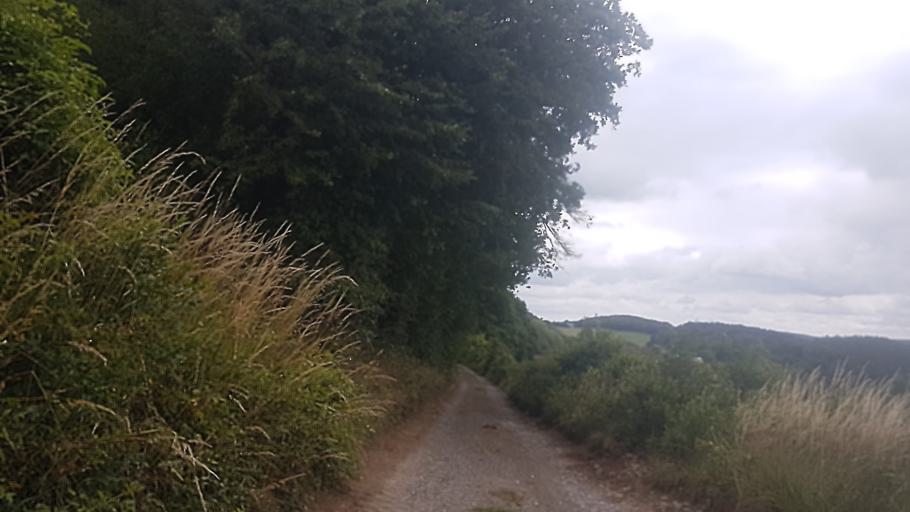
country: FR
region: Champagne-Ardenne
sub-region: Departement des Ardennes
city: Vireux-Molhain
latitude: 50.0827
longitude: 4.6224
